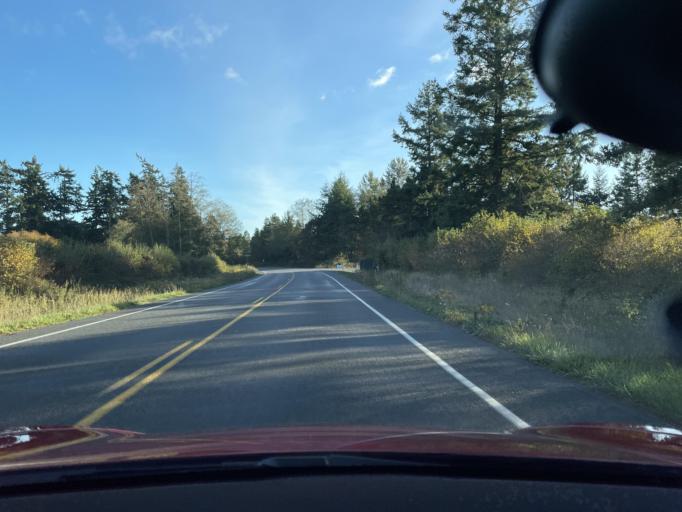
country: US
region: Washington
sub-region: San Juan County
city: Friday Harbor
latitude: 48.5044
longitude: -123.0361
